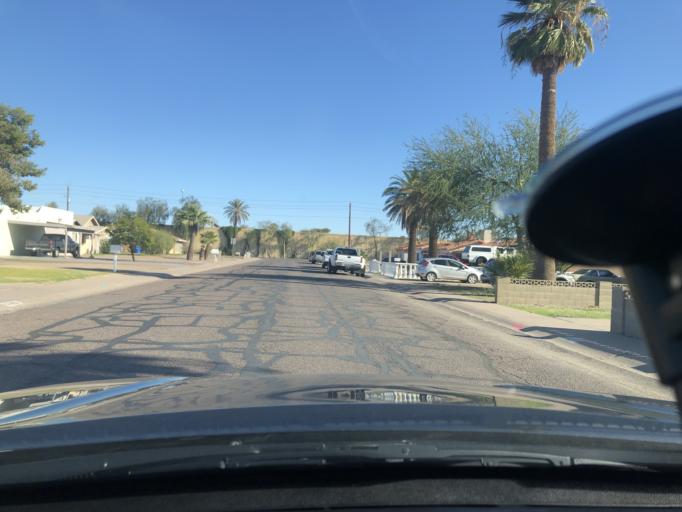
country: US
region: Arizona
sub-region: Maricopa County
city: Phoenix
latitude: 33.4694
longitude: -112.0403
